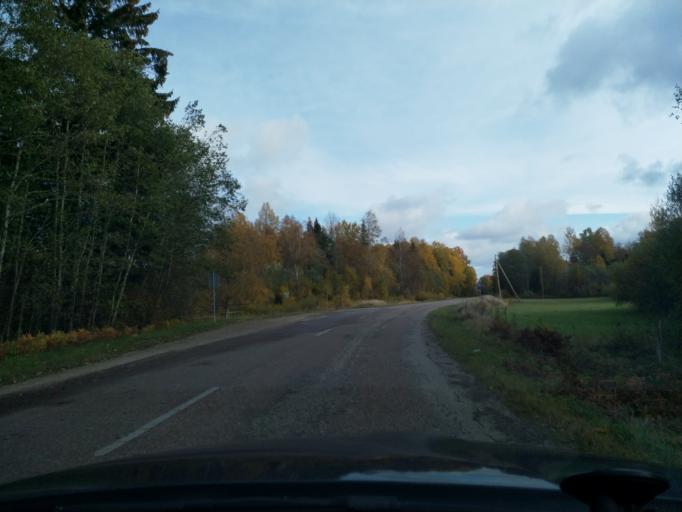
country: LV
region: Dundaga
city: Dundaga
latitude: 57.5514
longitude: 22.3581
